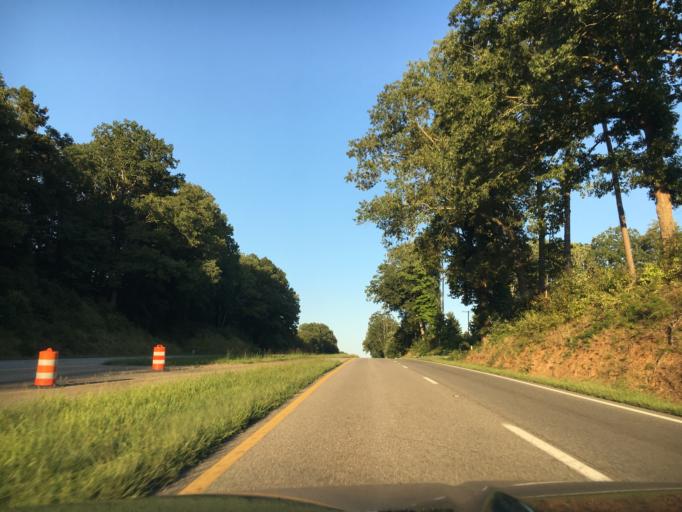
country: US
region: Virginia
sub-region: Halifax County
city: Mountain Road
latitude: 36.5832
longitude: -79.1525
